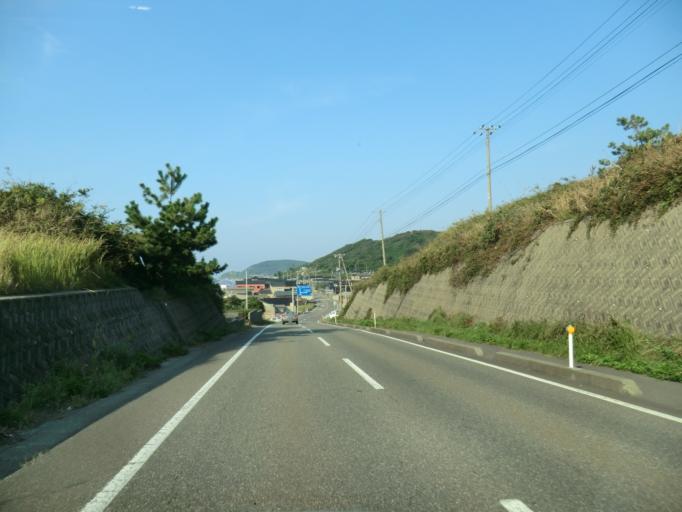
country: JP
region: Niigata
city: Kashiwazaki
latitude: 37.4540
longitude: 138.6088
